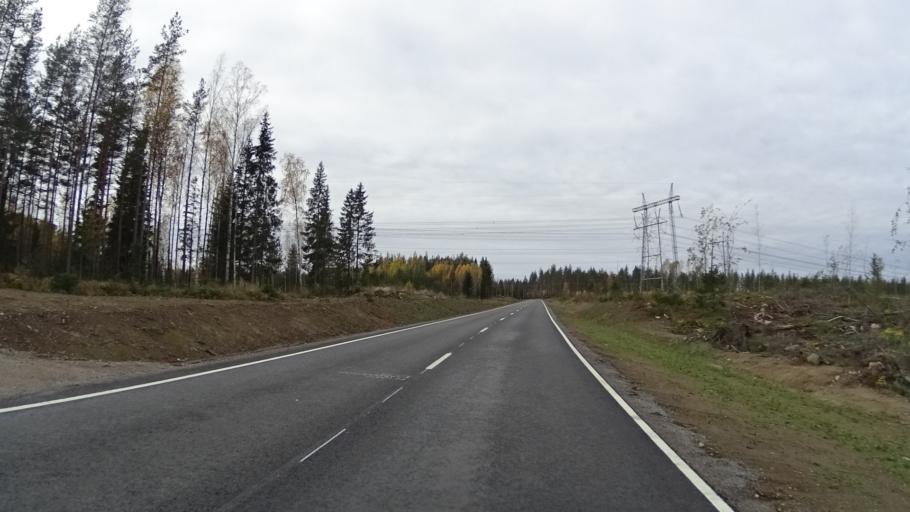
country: FI
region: South Karelia
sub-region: Lappeenranta
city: Taipalsaari
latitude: 61.0261
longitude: 28.0269
